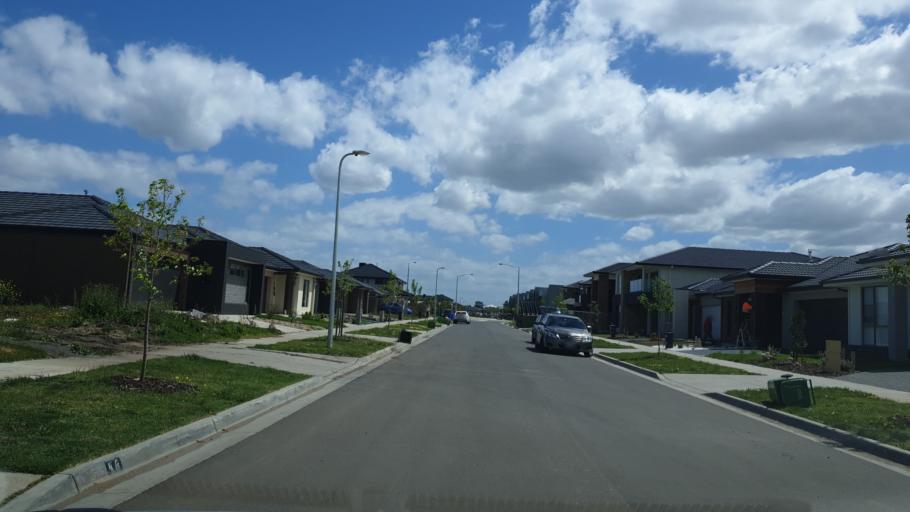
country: AU
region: Victoria
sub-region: Casey
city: Cranbourne
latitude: -38.0949
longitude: 145.3009
